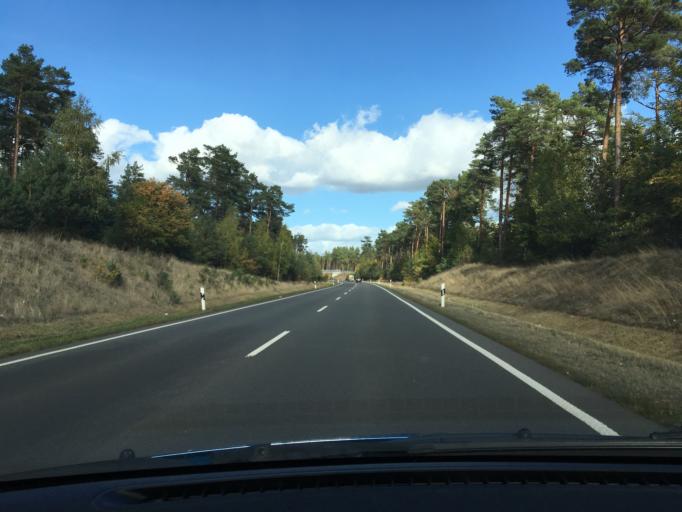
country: DE
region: Brandenburg
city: Perleberg
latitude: 53.0534
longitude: 11.8282
